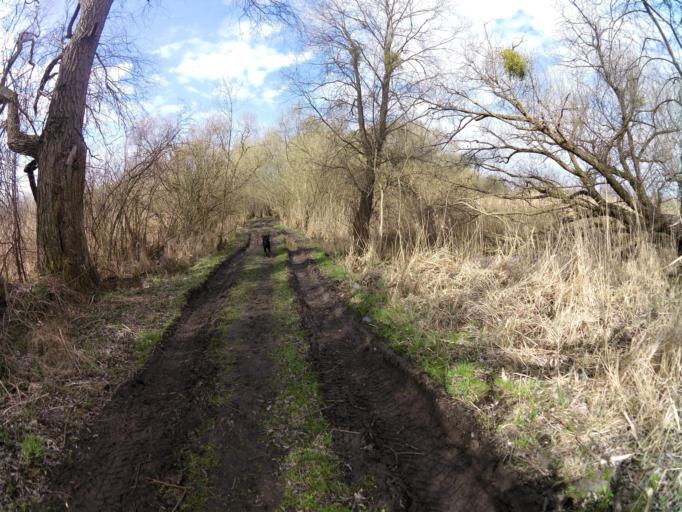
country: PL
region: West Pomeranian Voivodeship
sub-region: Powiat mysliborski
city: Mysliborz
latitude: 52.9365
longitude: 14.8625
